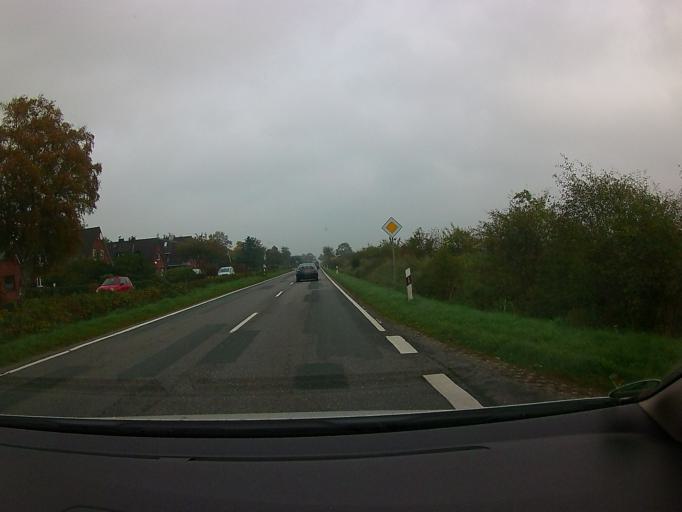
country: DE
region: Schleswig-Holstein
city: Wanderup
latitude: 54.6991
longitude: 9.3279
